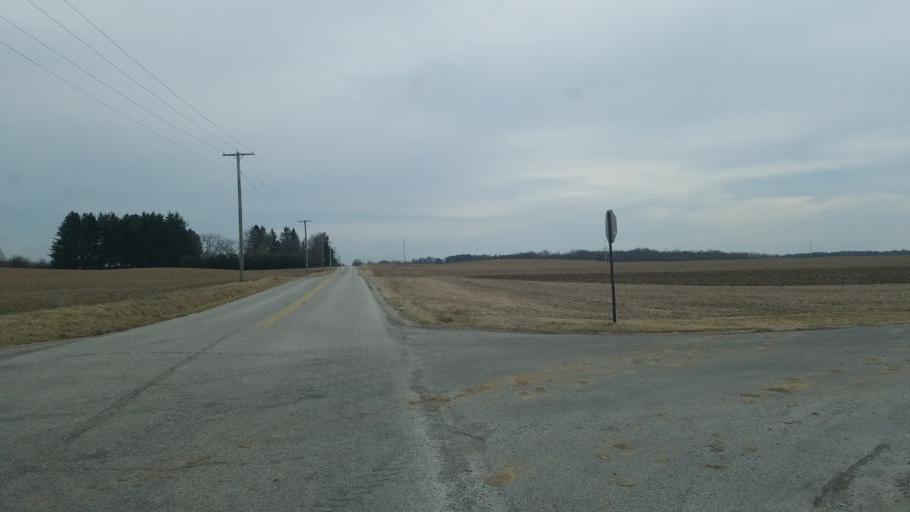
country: US
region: Ohio
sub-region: Richland County
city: Shelby
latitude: 40.8431
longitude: -82.6515
